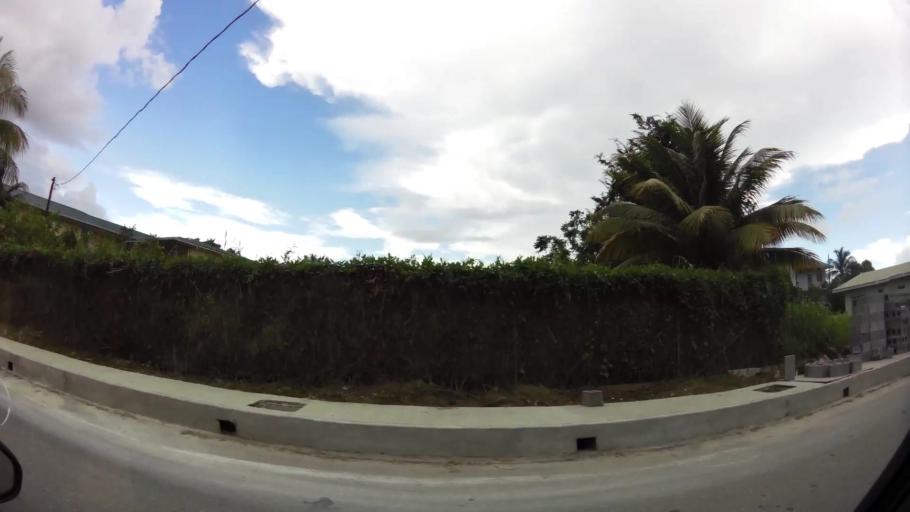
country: TT
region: City of San Fernando
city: Mon Repos
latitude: 10.2568
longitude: -61.4581
